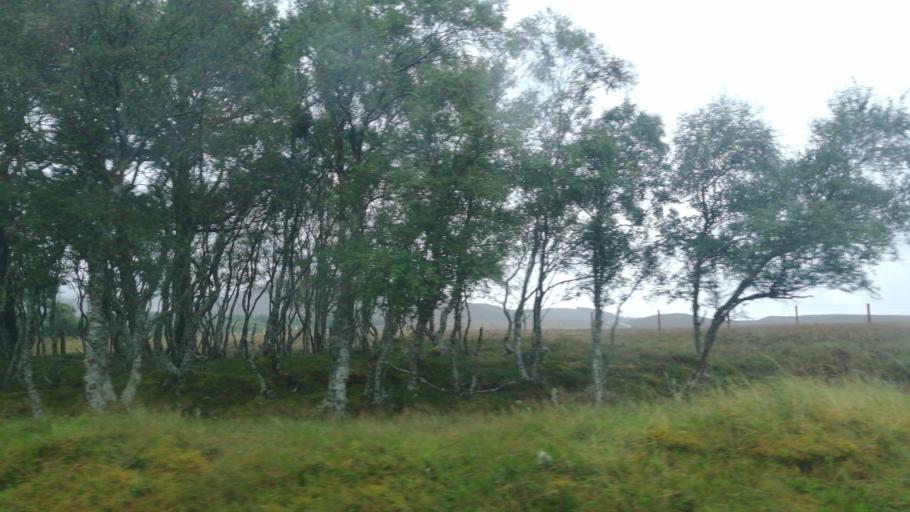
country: GB
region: Scotland
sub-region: Highland
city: Brora
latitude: 58.3565
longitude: -3.8996
